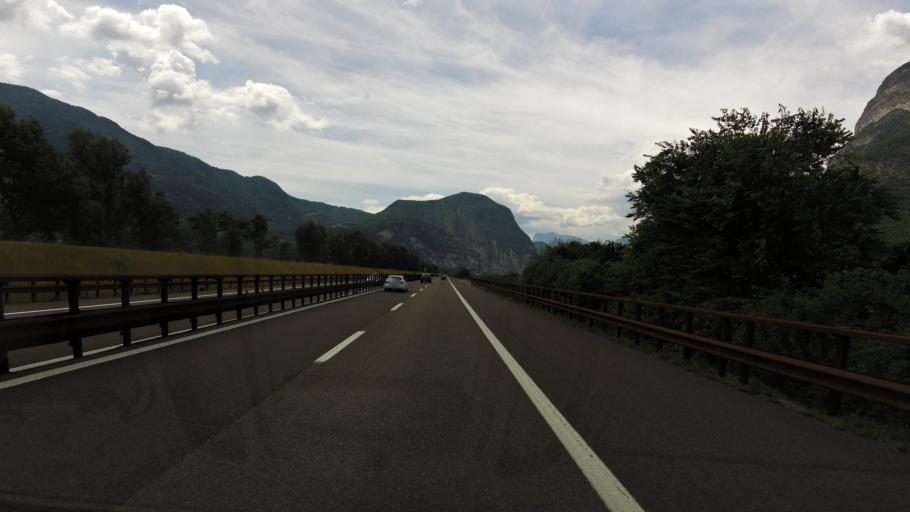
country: IT
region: Trentino-Alto Adige
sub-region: Bolzano
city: Cortina sulla Strada del Vino
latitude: 46.2624
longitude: 11.2263
